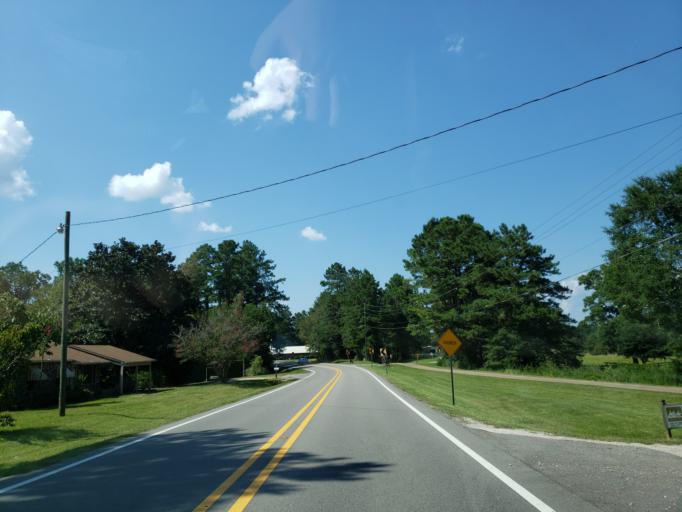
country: US
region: Mississippi
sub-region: Lamar County
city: Sumrall
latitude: 31.3999
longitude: -89.5418
